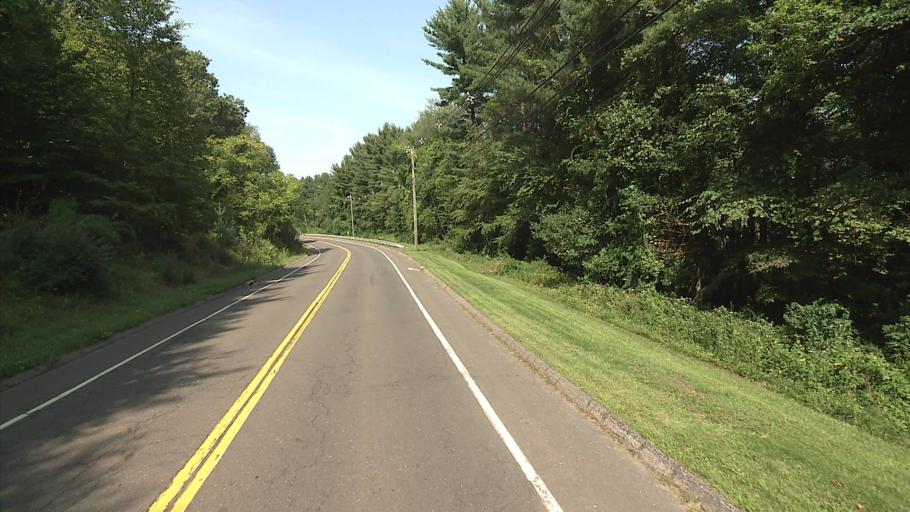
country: US
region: Connecticut
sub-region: Fairfield County
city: Newtown
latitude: 41.3992
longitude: -73.2746
